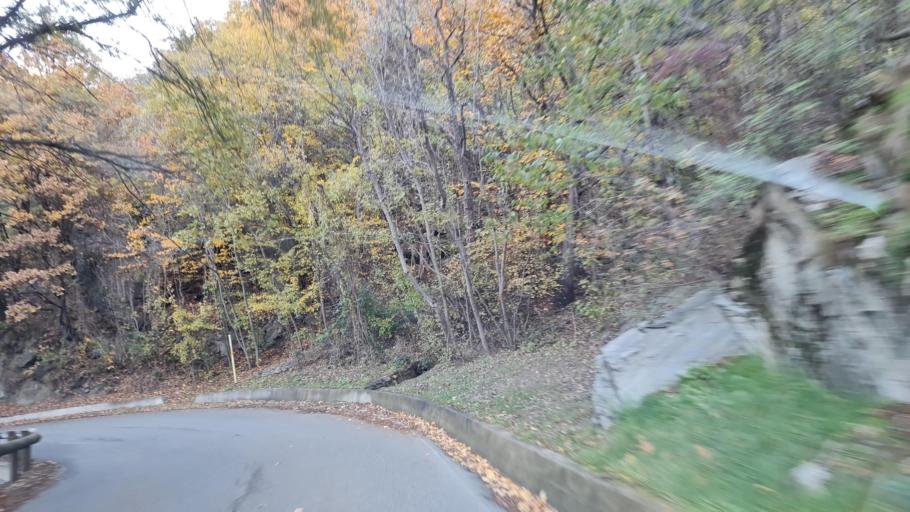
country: IT
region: Aosta Valley
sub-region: Valle d'Aosta
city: Montjovet
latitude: 45.7291
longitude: 7.6672
